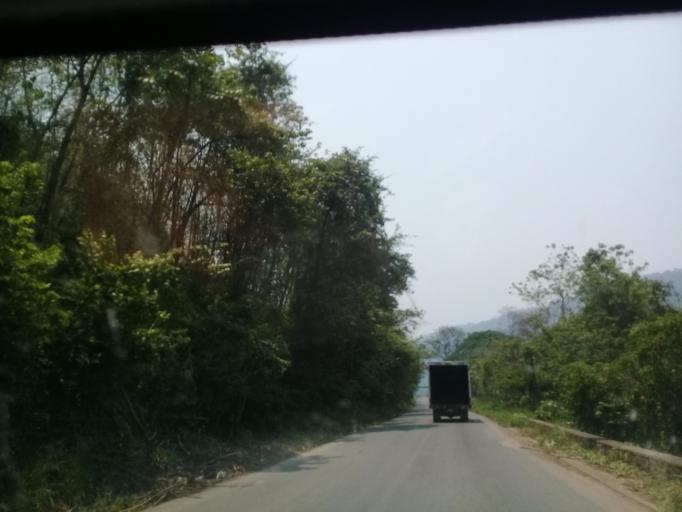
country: MX
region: Veracruz
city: Tezonapa
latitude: 18.6082
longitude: -96.6921
